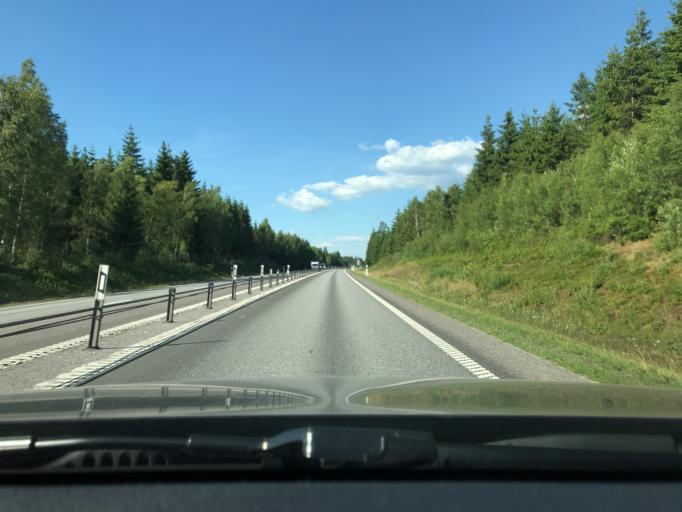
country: SE
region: Skane
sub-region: Osby Kommun
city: Osby
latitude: 56.4336
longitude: 14.0619
